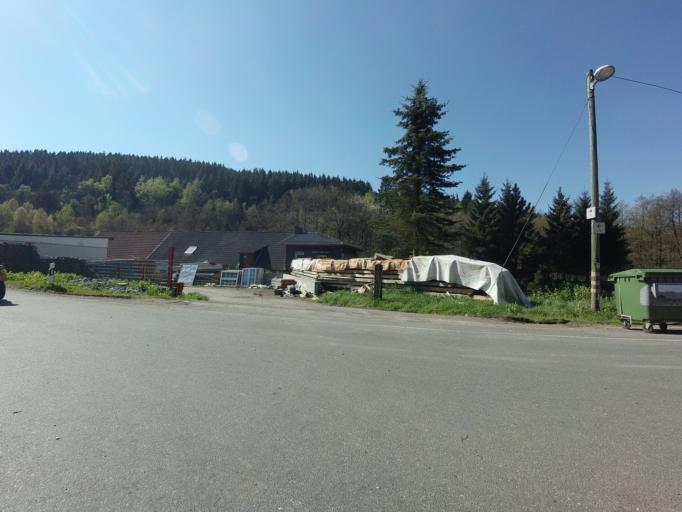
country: DE
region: North Rhine-Westphalia
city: Meinerzhagen
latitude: 51.1084
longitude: 7.7141
